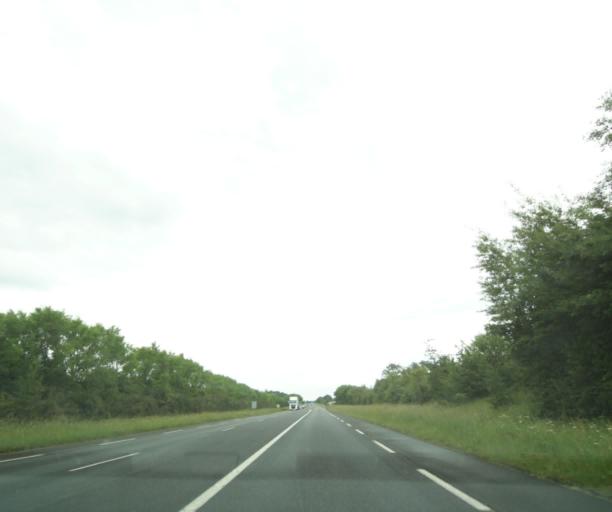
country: FR
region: Poitou-Charentes
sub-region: Departement des Deux-Sevres
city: Airvault
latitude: 46.7959
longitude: -0.2134
